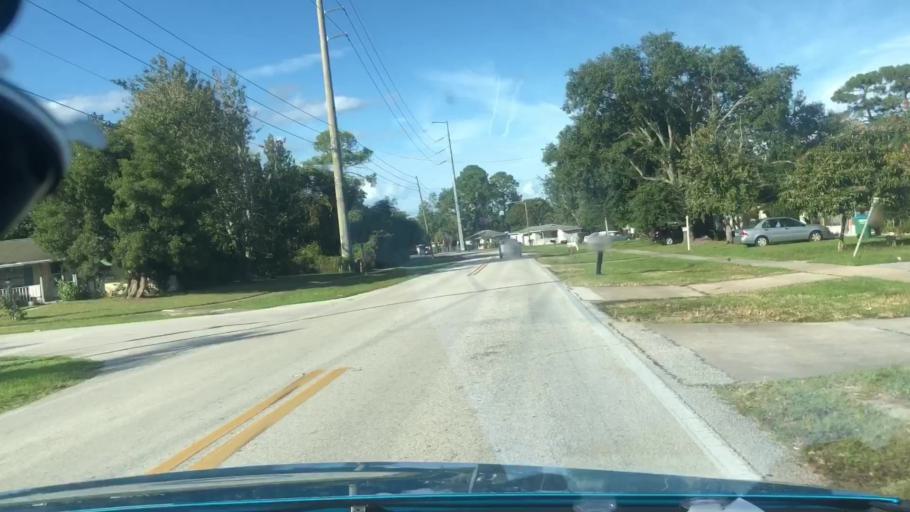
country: US
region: Florida
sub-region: Volusia County
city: Deltona
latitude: 28.8938
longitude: -81.2331
